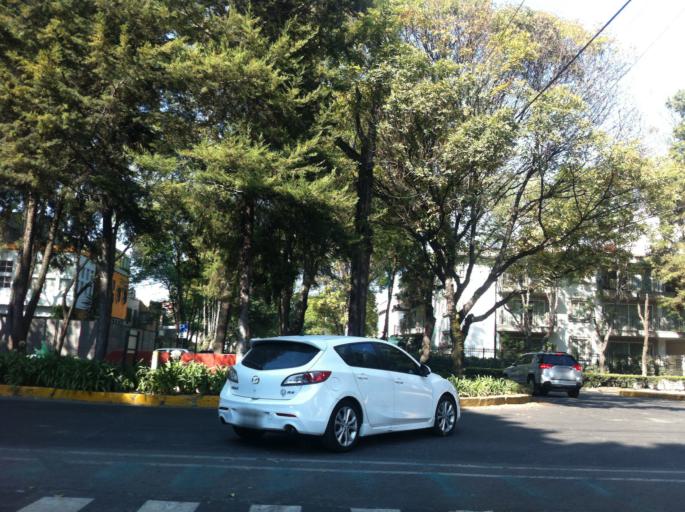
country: MX
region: Mexico City
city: Miguel Hidalgo
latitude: 19.4336
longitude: -99.1933
